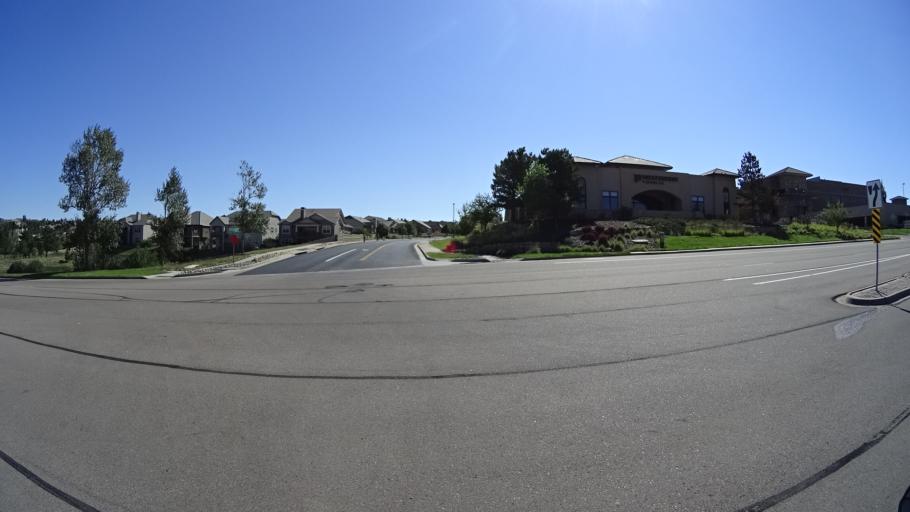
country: US
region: Colorado
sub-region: El Paso County
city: Air Force Academy
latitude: 38.9688
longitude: -104.7852
